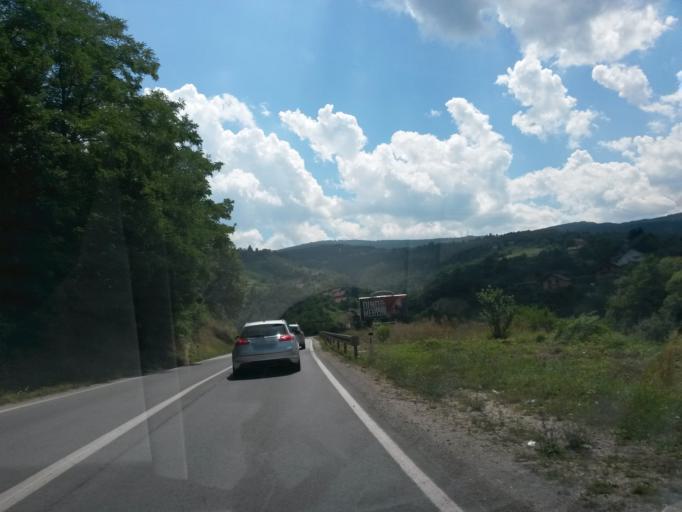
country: BA
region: Federation of Bosnia and Herzegovina
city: Turbe
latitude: 44.2353
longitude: 17.6111
